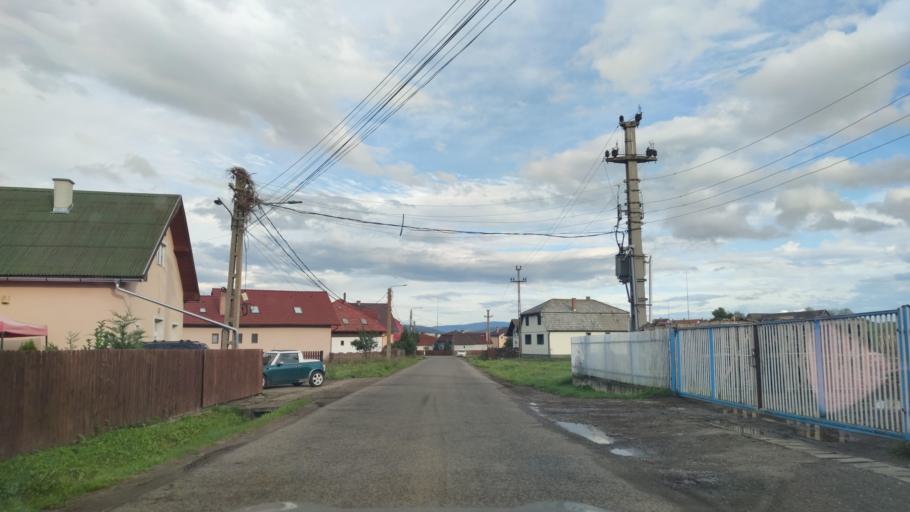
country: RO
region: Harghita
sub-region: Comuna Remetea
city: Remetea
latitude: 46.8013
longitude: 25.4404
